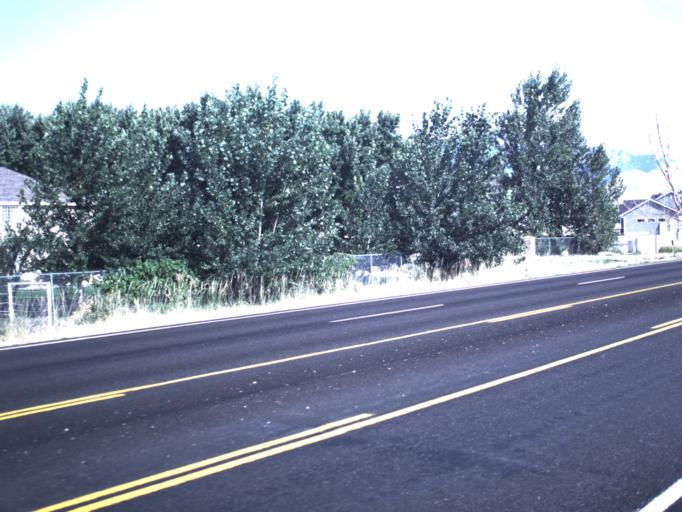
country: US
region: Utah
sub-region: Weber County
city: Farr West
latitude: 41.3307
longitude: -112.0239
